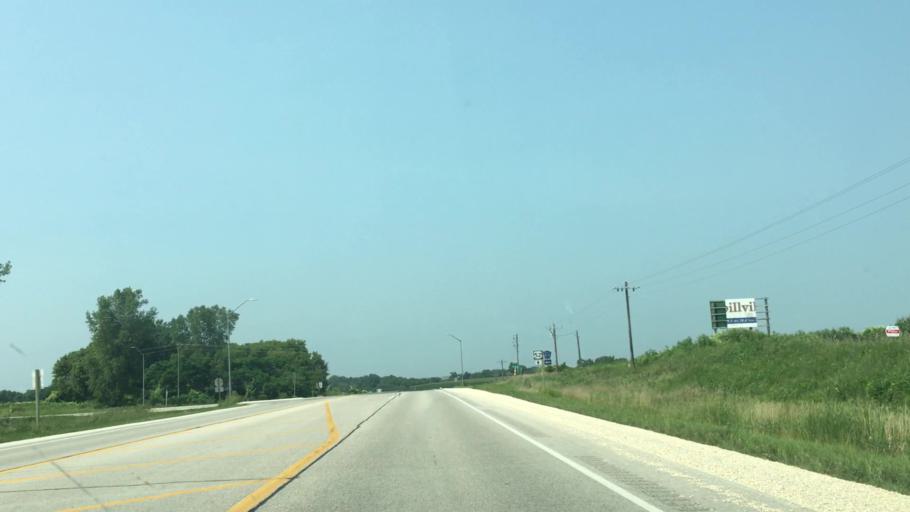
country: US
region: Iowa
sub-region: Winneshiek County
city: Decorah
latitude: 43.2045
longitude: -91.8778
